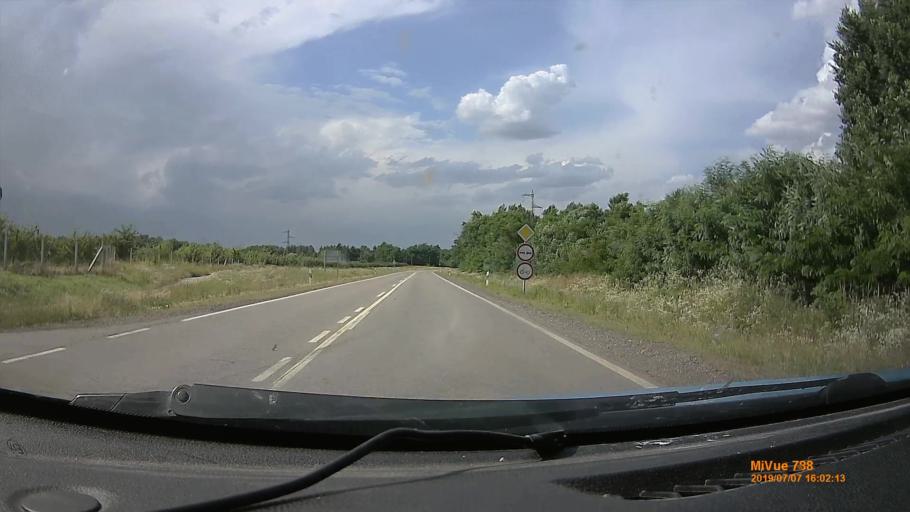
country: HU
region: Heves
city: Boldog
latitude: 47.6209
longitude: 19.7319
